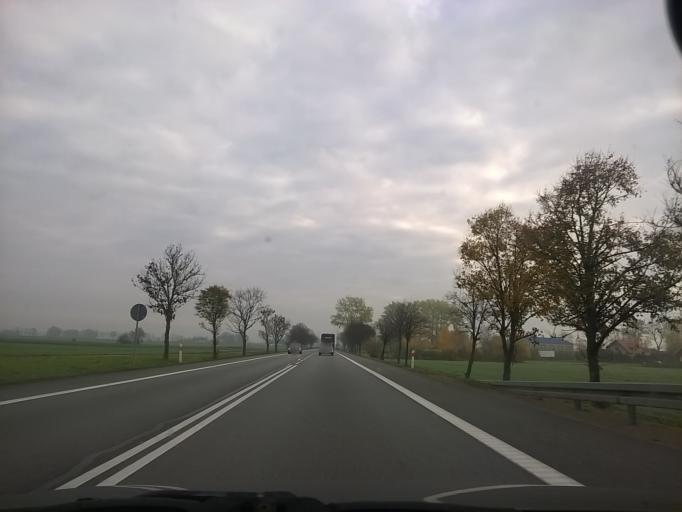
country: PL
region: Pomeranian Voivodeship
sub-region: Powiat nowodworski
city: Nowy Dwor Gdanski
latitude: 54.1915
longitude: 19.1550
